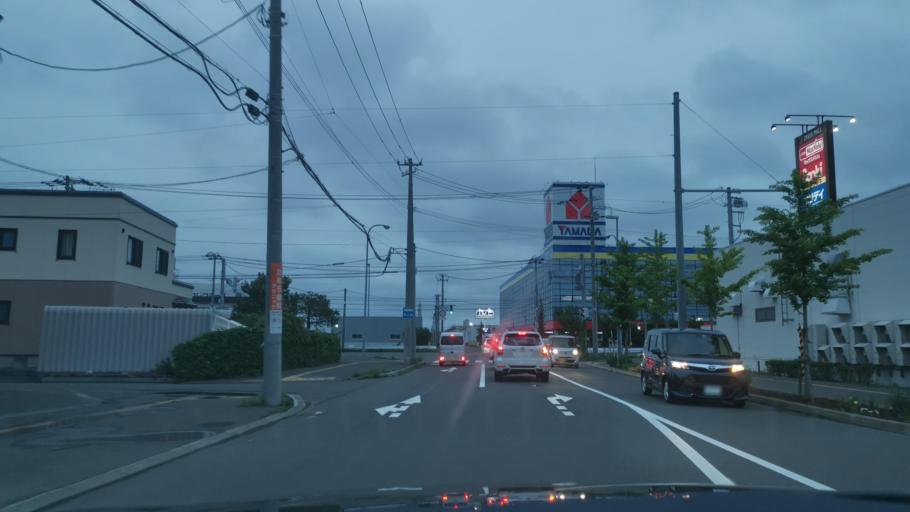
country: JP
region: Hokkaido
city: Sapporo
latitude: 43.1066
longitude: 141.2739
